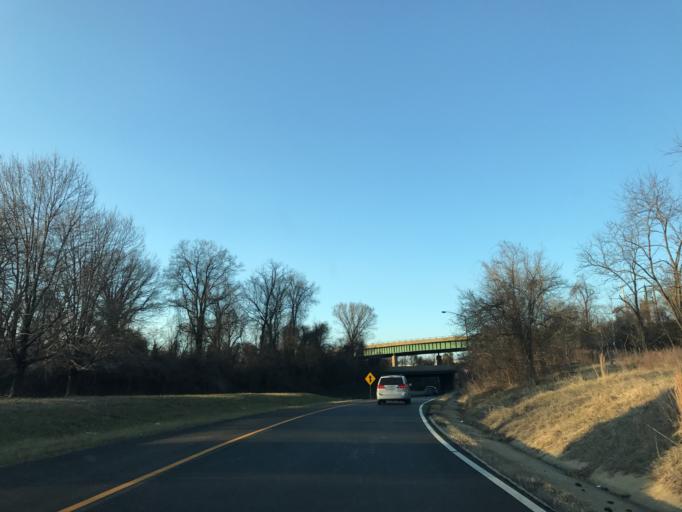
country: US
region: Maryland
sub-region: Anne Arundel County
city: Arnold
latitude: 39.0128
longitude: -76.4905
